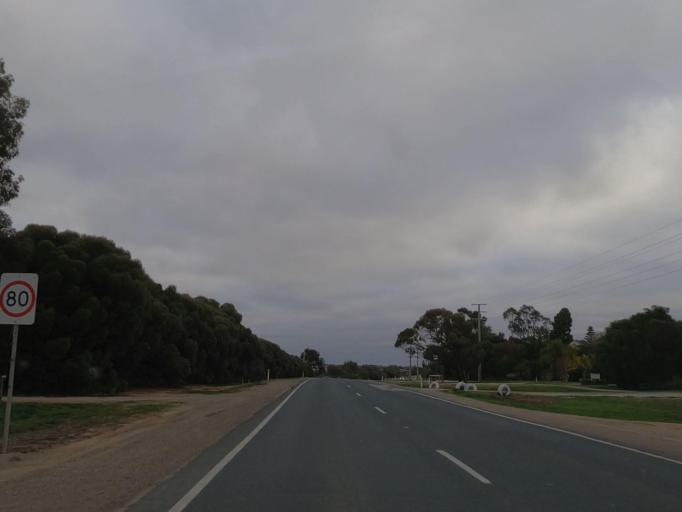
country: AU
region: Victoria
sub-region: Swan Hill
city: Swan Hill
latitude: -35.4668
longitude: 143.6526
